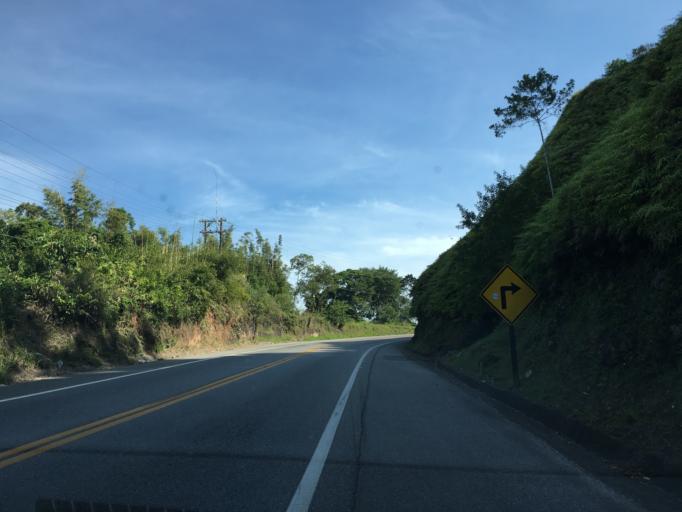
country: BR
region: Sao Paulo
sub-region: Sao Sebastiao
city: Sao Sebastiao
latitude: -23.7721
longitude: -45.7185
